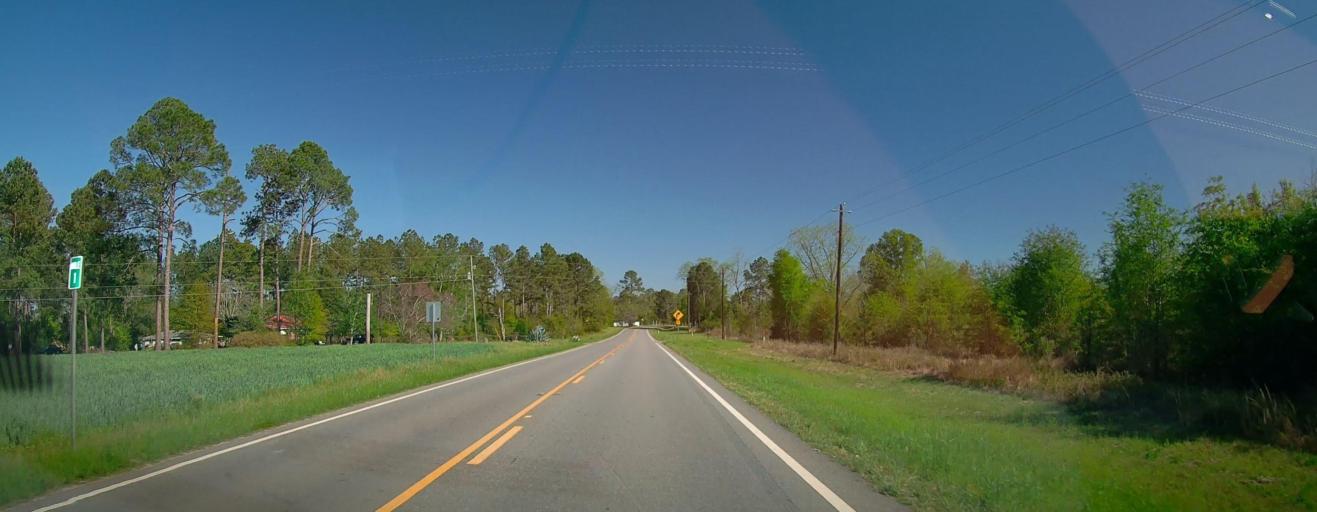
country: US
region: Georgia
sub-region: Pulaski County
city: Hawkinsville
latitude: 32.1320
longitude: -83.5034
